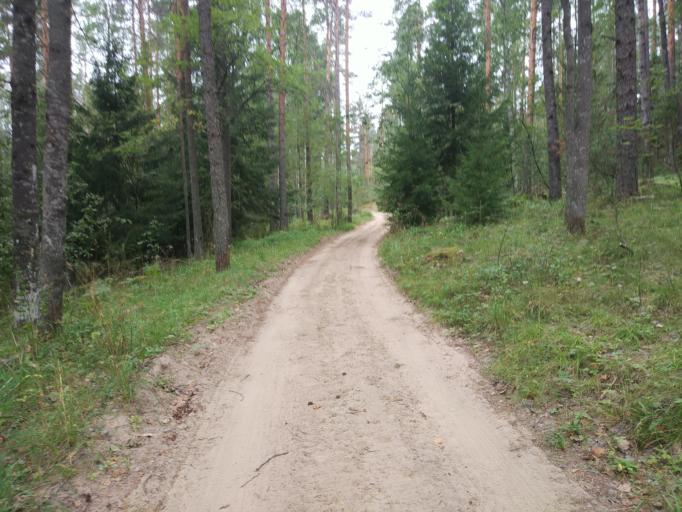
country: RU
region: Leningrad
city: Kuznechnoye
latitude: 61.0114
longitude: 29.6467
